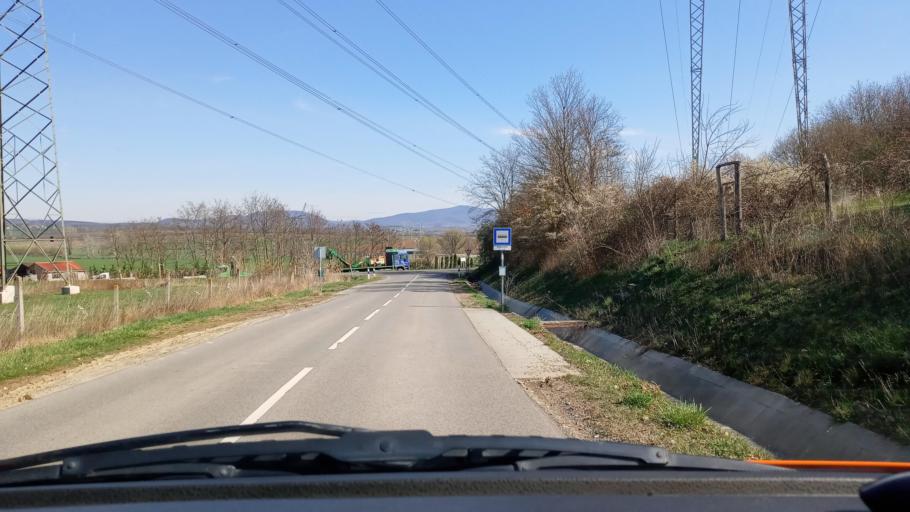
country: HU
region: Baranya
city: Kozarmisleny
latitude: 46.0834
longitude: 18.3077
